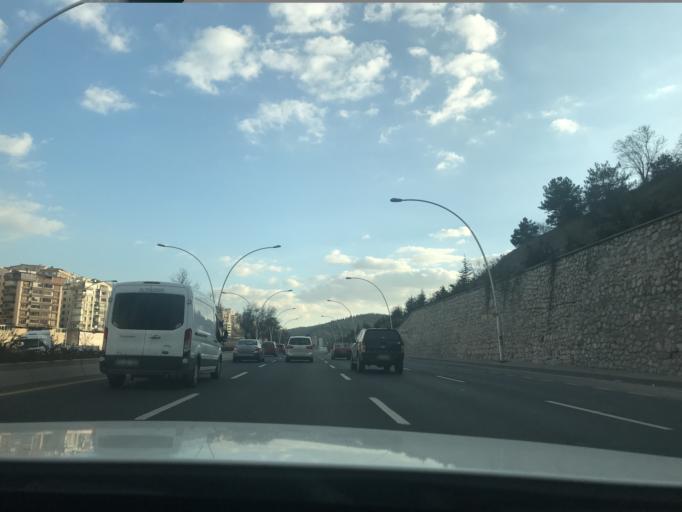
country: TR
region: Ankara
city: Ankara
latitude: 39.8728
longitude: 32.8109
